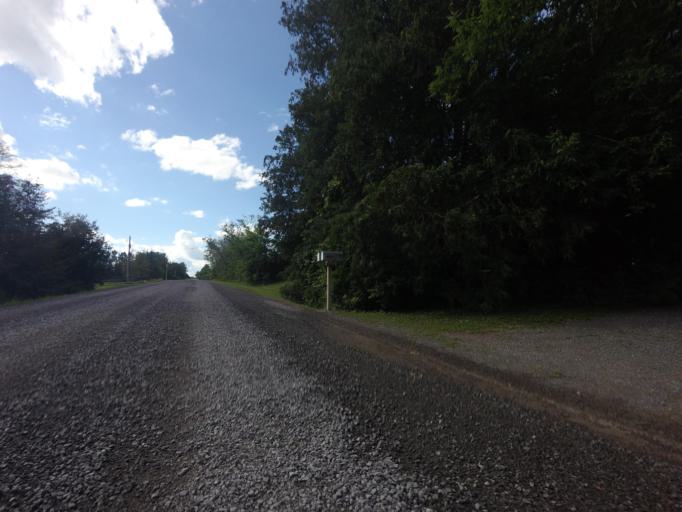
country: CA
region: Ontario
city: Arnprior
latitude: 45.3366
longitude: -76.1888
